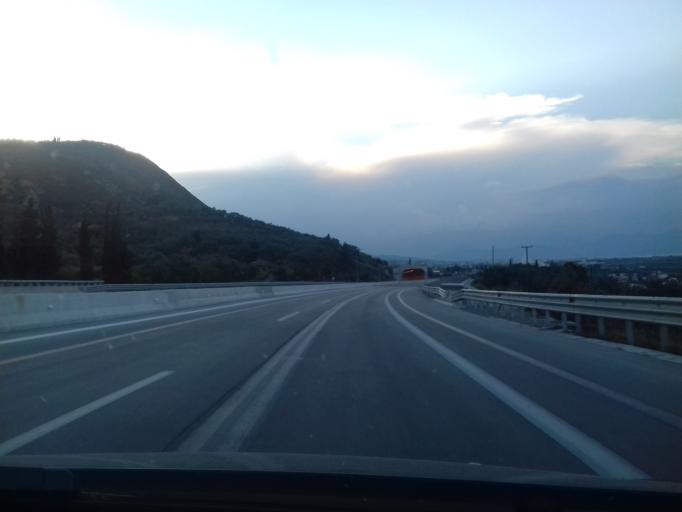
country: GR
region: West Greece
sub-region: Nomos Achaias
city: Temeni
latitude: 38.2057
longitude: 22.1398
